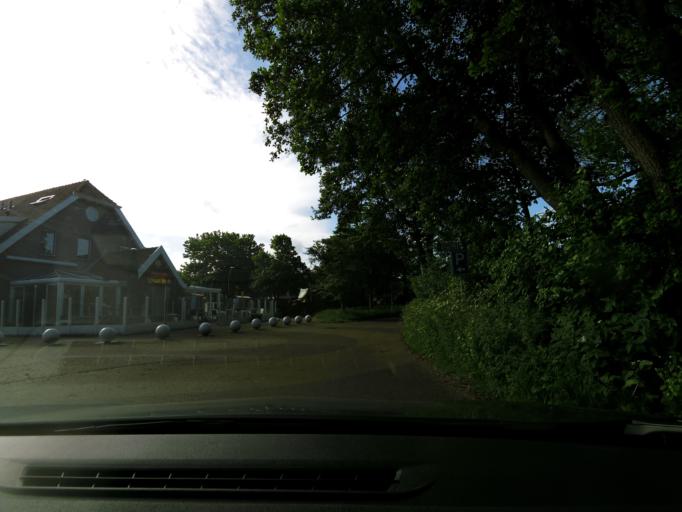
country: NL
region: Zeeland
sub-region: Schouwen-Duiveland
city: Renesse
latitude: 51.7411
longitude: 3.7843
